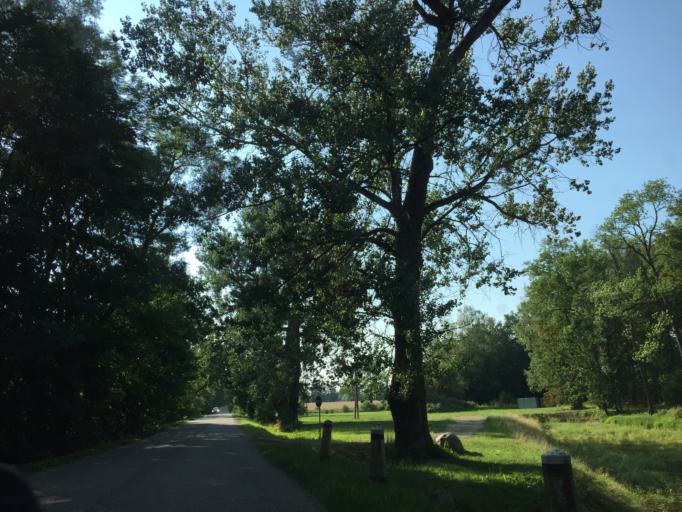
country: LT
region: Siauliu apskritis
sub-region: Joniskis
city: Joniskis
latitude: 56.4230
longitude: 23.6971
